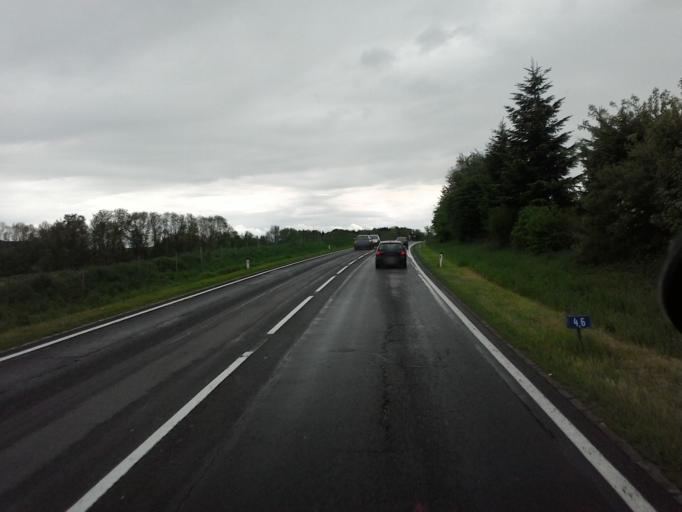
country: AT
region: Upper Austria
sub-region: Wels-Land
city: Thalheim bei Wels
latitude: 48.1256
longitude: 14.0510
